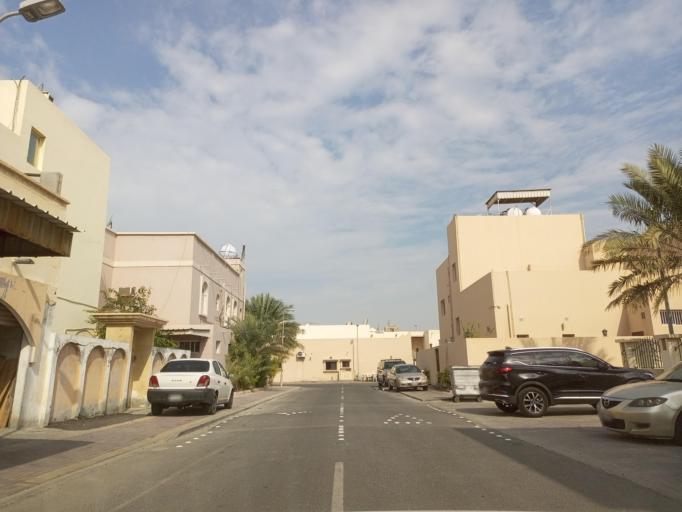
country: BH
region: Muharraq
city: Al Hadd
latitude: 26.2554
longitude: 50.6418
